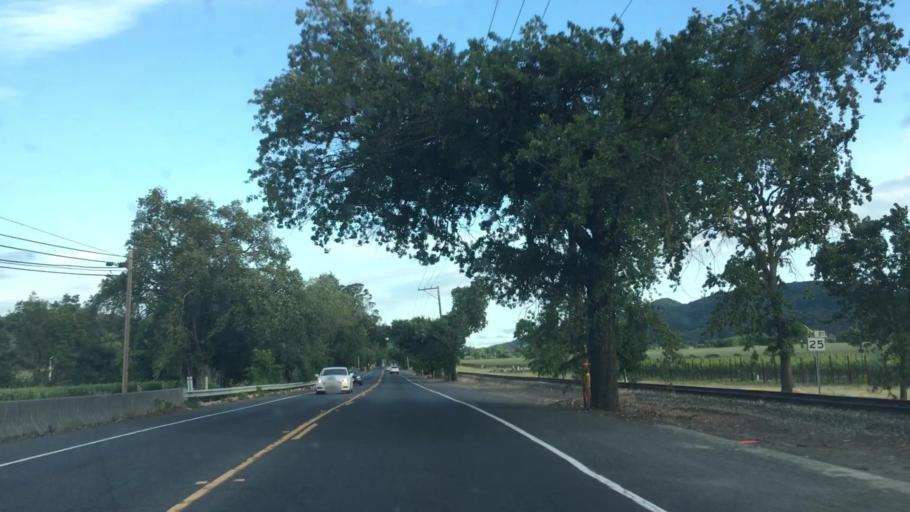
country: US
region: California
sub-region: Napa County
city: Yountville
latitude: 38.4320
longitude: -122.3984
